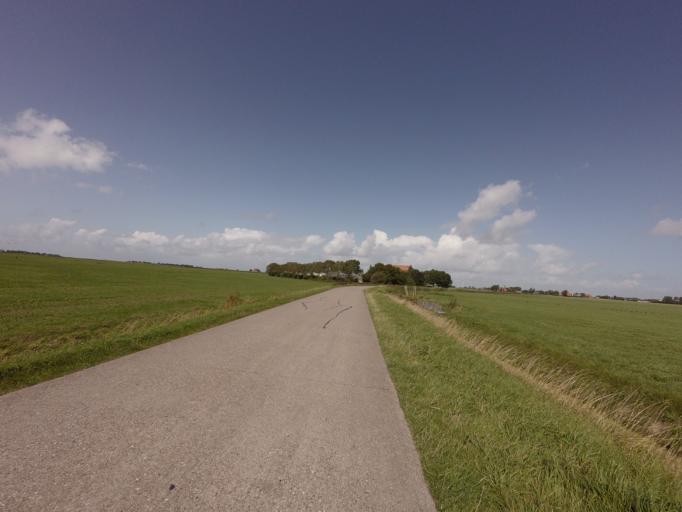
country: NL
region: Friesland
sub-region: Sudwest Fryslan
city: Makkum
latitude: 53.0688
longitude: 5.4554
